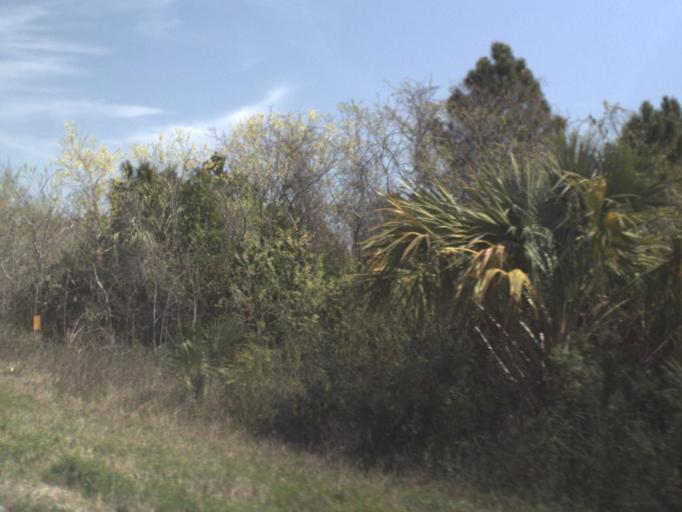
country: US
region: Florida
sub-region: Gulf County
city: Port Saint Joe
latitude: 29.6746
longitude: -85.3467
